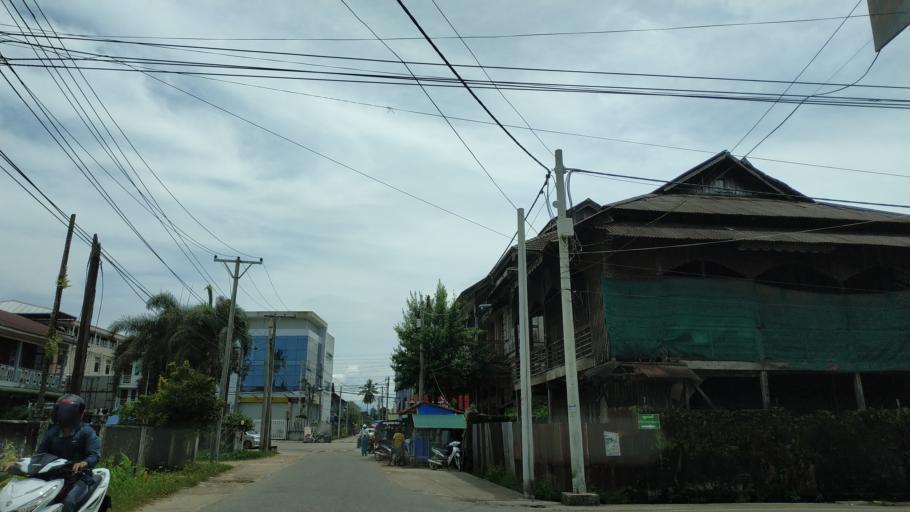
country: MM
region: Tanintharyi
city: Dawei
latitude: 14.0749
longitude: 98.1882
